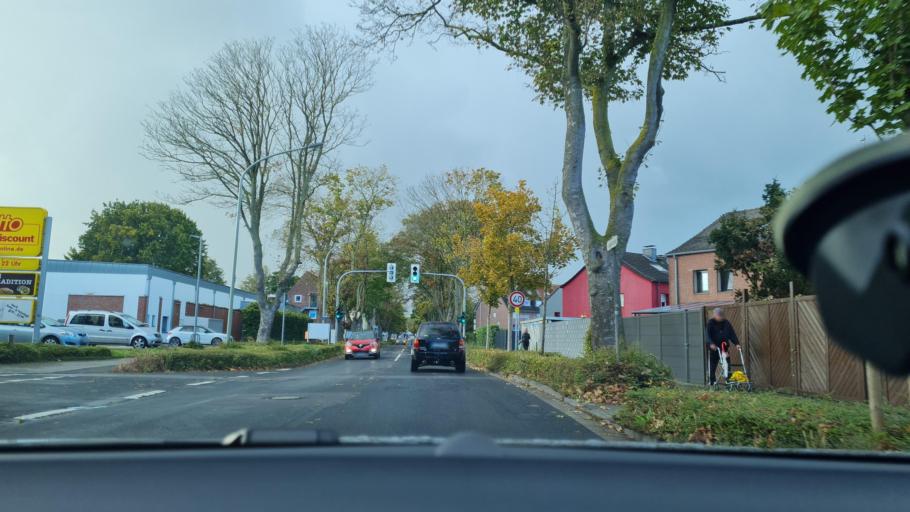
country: DE
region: North Rhine-Westphalia
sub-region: Regierungsbezirk Dusseldorf
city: Dinslaken
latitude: 51.5798
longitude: 6.7372
